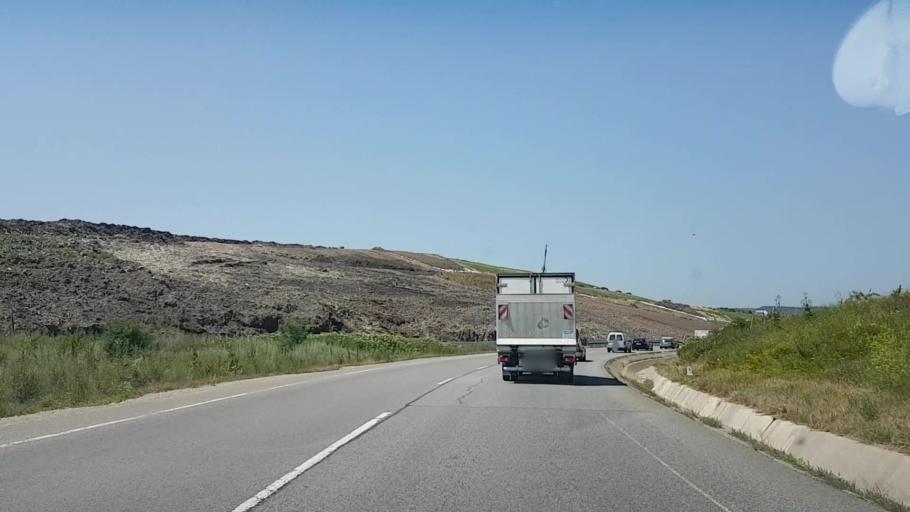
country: RO
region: Cluj
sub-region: Comuna Apahida
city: Dezmir
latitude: 46.7630
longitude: 23.6908
